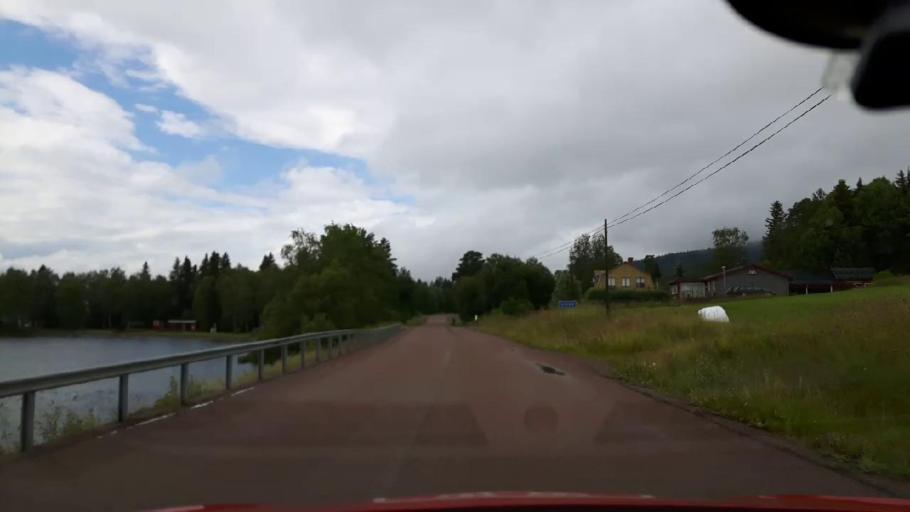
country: SE
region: Jaemtland
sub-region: Krokoms Kommun
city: Valla
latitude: 63.3748
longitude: 14.0233
